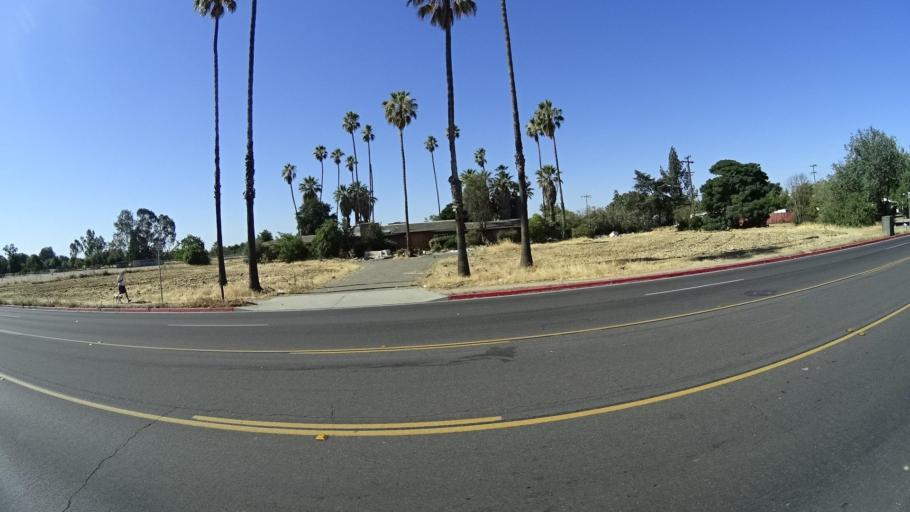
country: US
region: California
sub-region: Fresno County
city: Sunnyside
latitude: 36.7576
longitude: -119.7087
